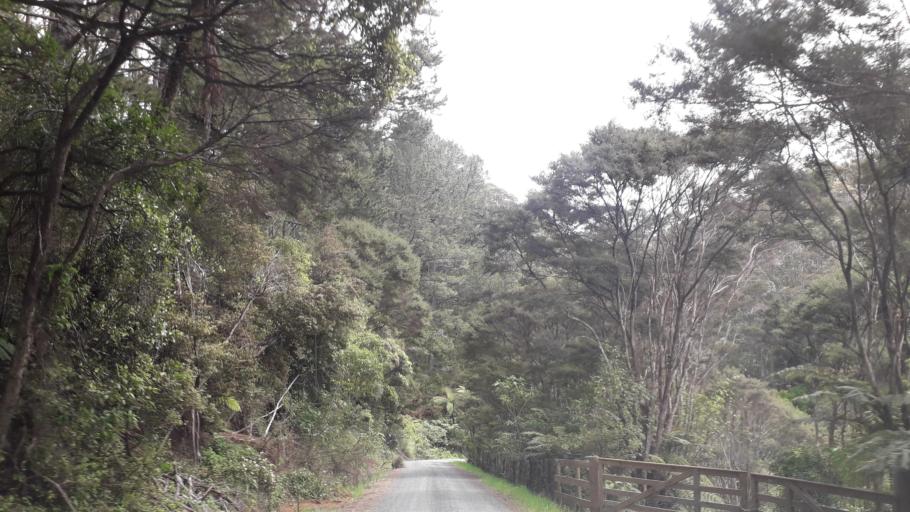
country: NZ
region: Northland
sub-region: Far North District
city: Taipa
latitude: -35.0899
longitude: 173.5511
